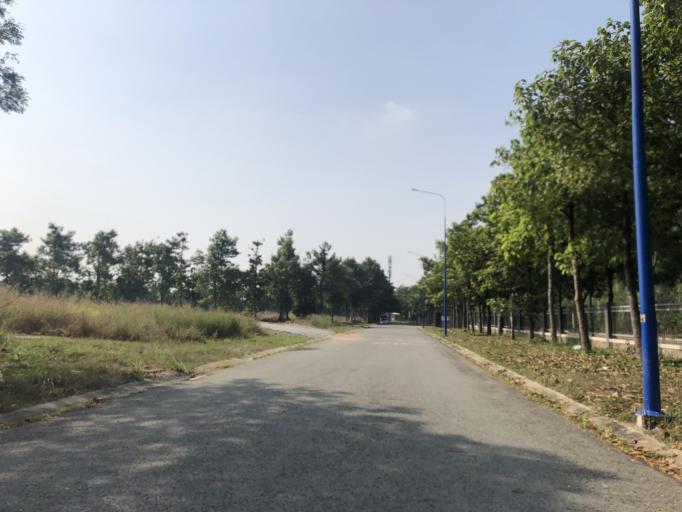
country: VN
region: Binh Duong
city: Thu Dau Mot
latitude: 11.0535
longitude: 106.6642
